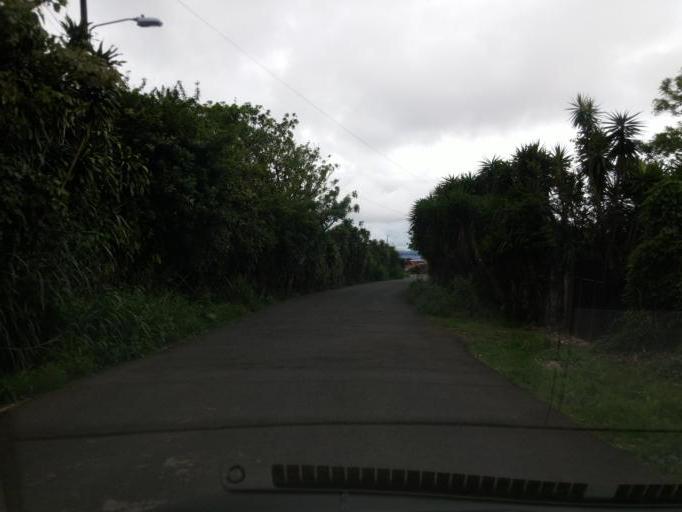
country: CR
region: Heredia
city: Mercedes
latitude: 10.0255
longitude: -84.1307
